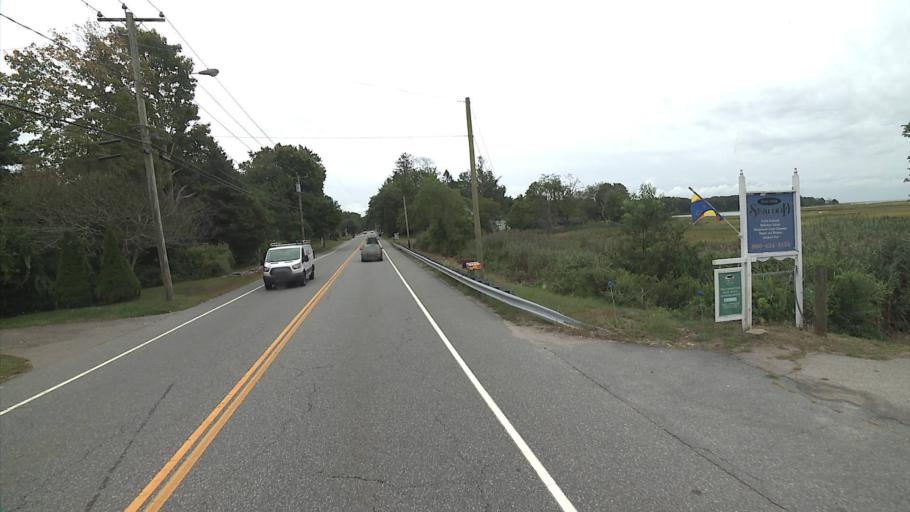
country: US
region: Connecticut
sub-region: Middlesex County
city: Old Saybrook Center
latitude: 41.2927
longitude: -72.3142
